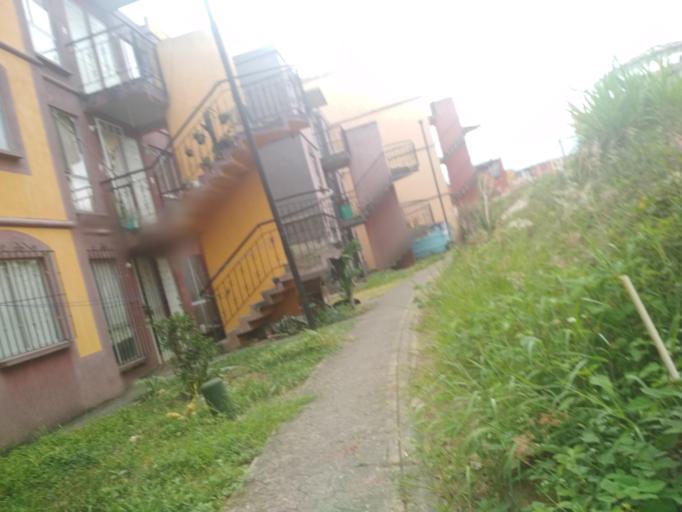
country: MX
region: Veracruz
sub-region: Coatepec
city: Las Lomas
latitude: 19.4167
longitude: -96.9276
